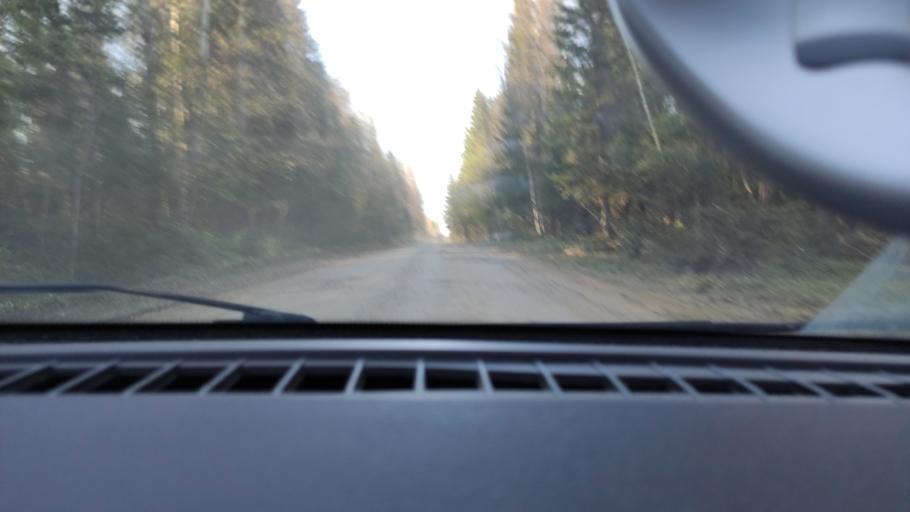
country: RU
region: Perm
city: Polazna
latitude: 58.1294
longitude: 56.4578
